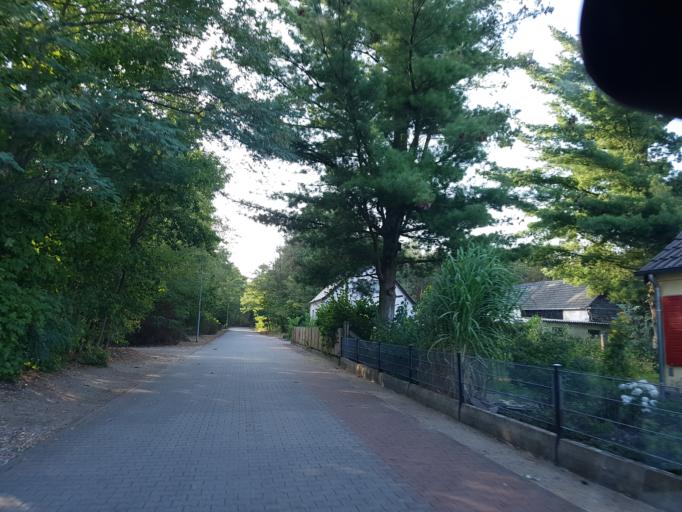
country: DE
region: Saxony-Anhalt
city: Holzdorf
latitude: 51.7582
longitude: 13.1319
